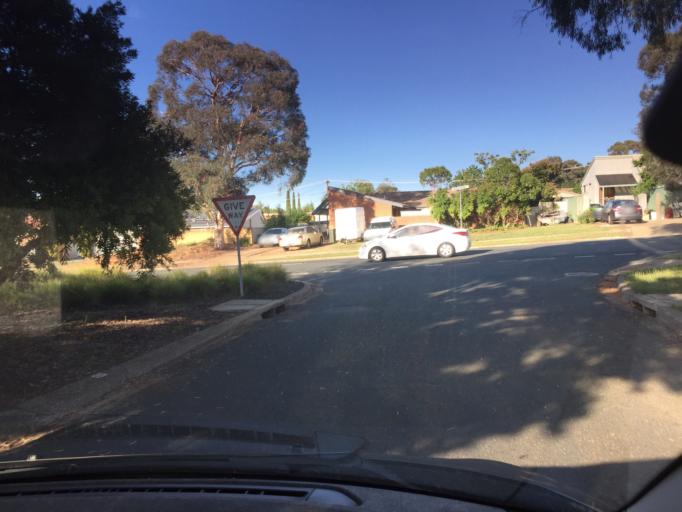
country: AU
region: Australian Capital Territory
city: Kaleen
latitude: -35.2196
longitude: 149.1115
